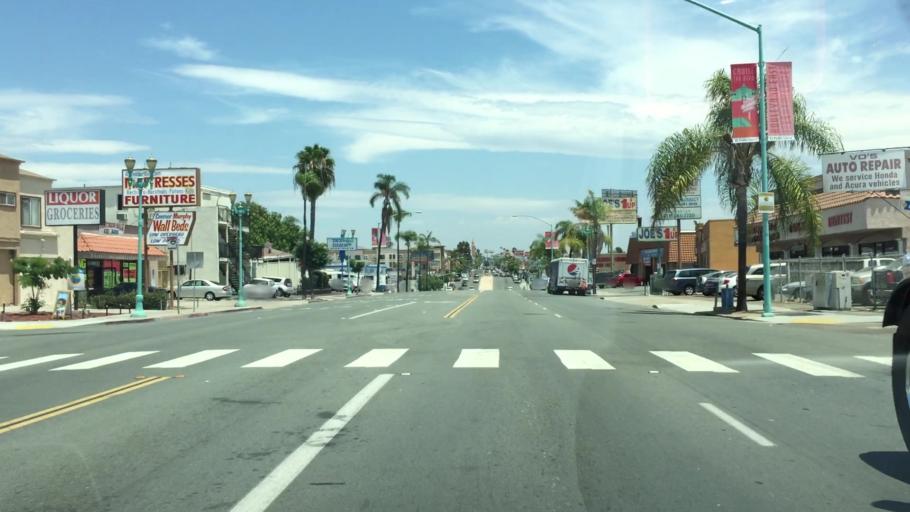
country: US
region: California
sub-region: San Diego County
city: Lemon Grove
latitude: 32.7569
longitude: -117.0859
